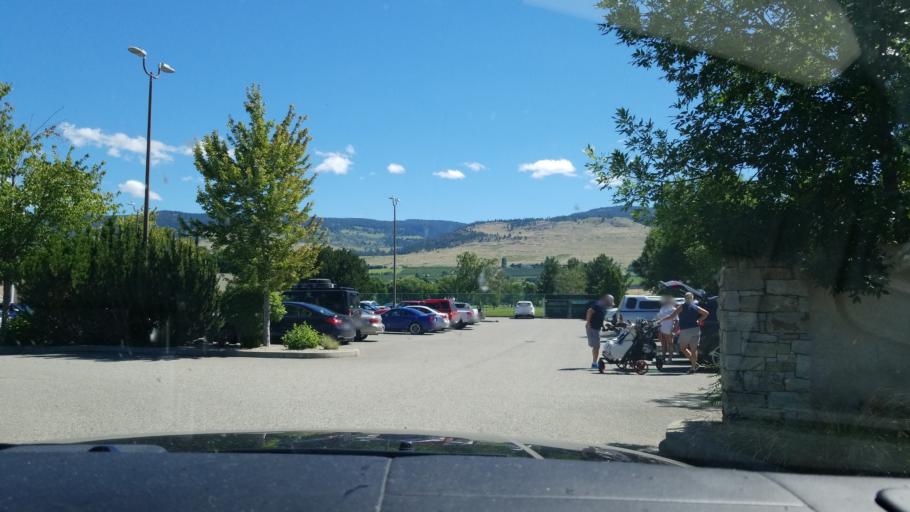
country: CA
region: British Columbia
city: Kelowna
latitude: 49.9219
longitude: -119.3789
